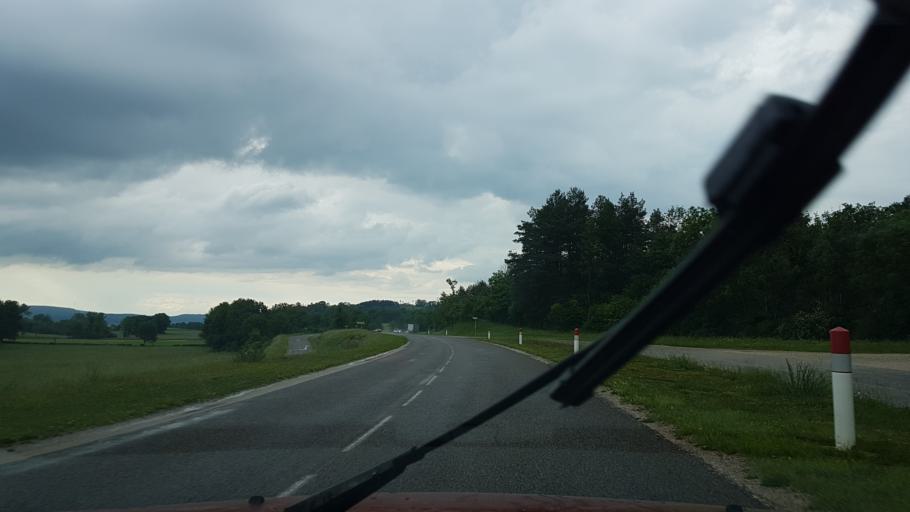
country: FR
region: Franche-Comte
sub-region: Departement du Jura
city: Clairvaux-les-Lacs
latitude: 46.5538
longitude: 5.7454
